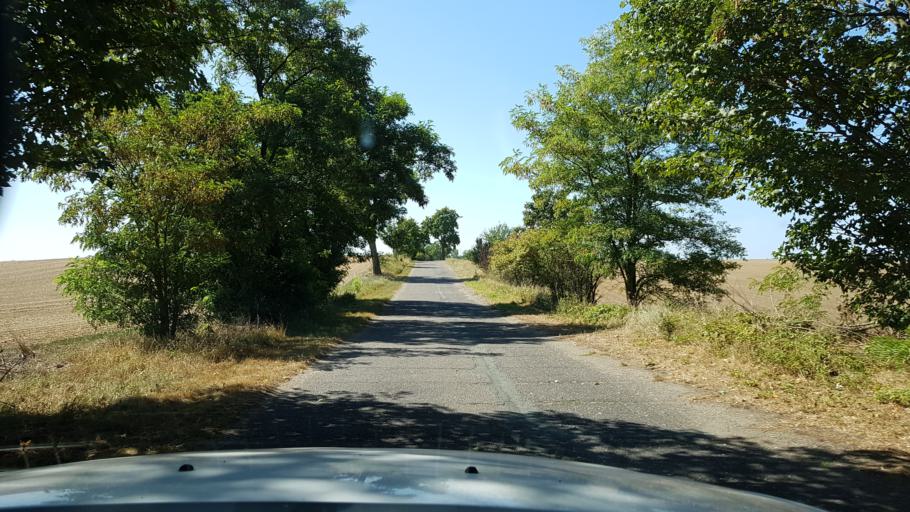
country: PL
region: West Pomeranian Voivodeship
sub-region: Powiat gryfinski
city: Moryn
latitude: 52.8454
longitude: 14.3759
